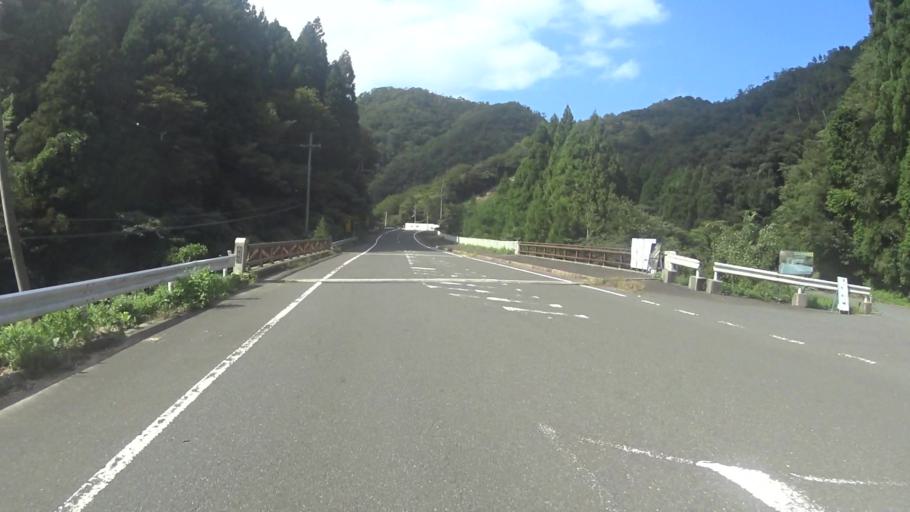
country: JP
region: Kyoto
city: Miyazu
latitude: 35.7353
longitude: 135.2552
